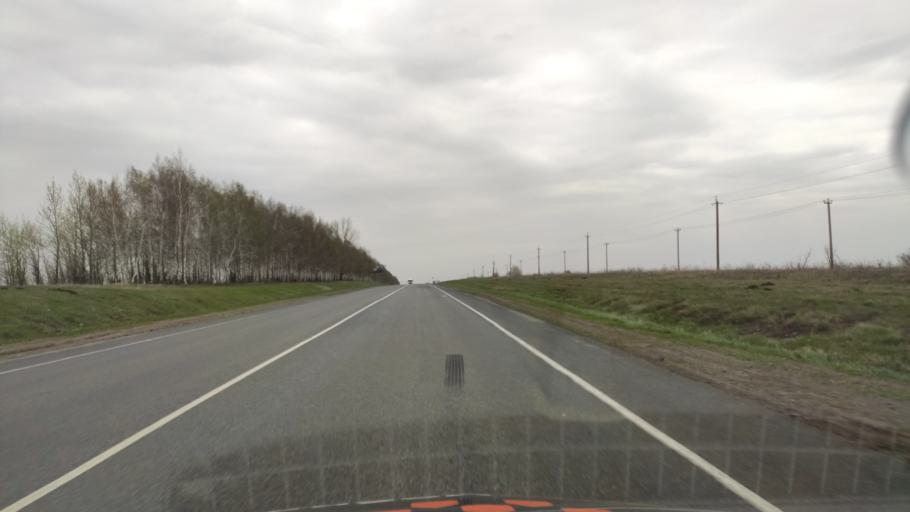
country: RU
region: Kursk
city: Gorshechnoye
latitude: 51.5025
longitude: 37.9877
